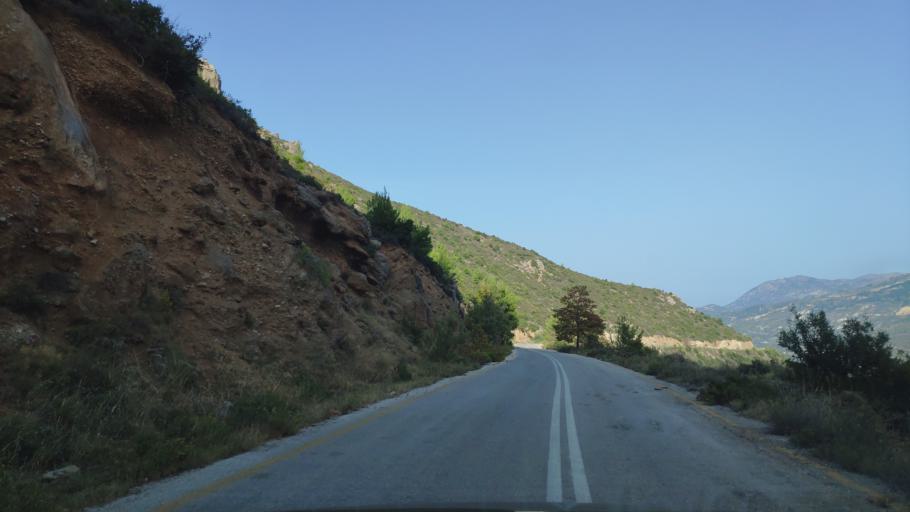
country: GR
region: West Greece
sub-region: Nomos Achaias
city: Aiyira
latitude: 38.0680
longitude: 22.3792
